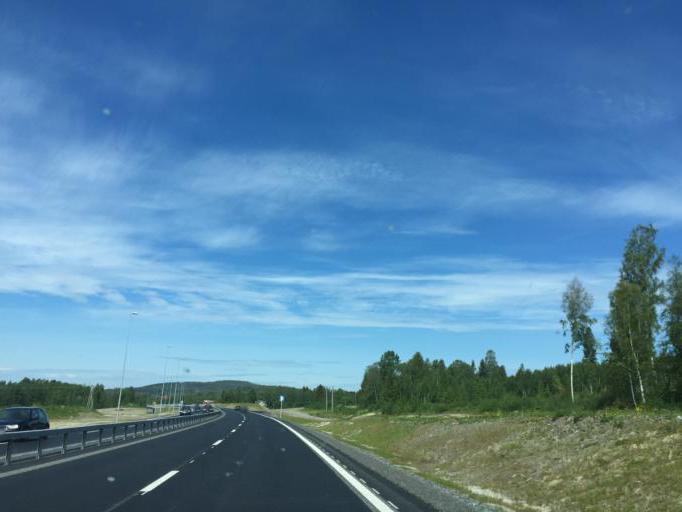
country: NO
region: Hedmark
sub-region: Kongsvinger
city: Spetalen
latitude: 60.2273
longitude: 11.8565
